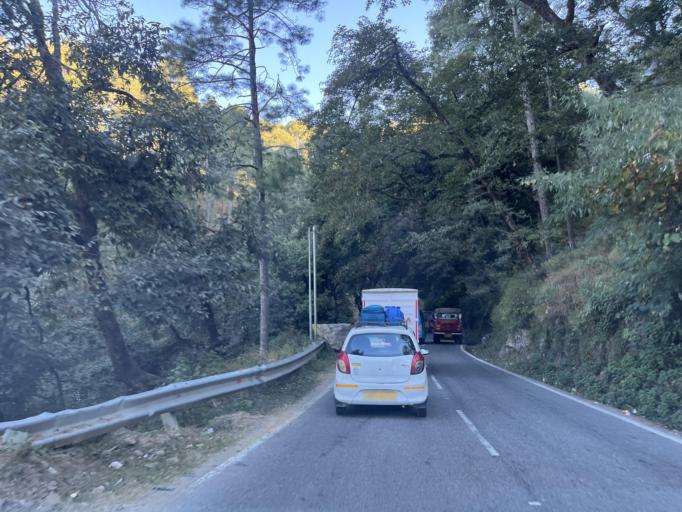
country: IN
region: Uttarakhand
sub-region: Naini Tal
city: Bhowali
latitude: 29.3971
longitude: 79.5111
